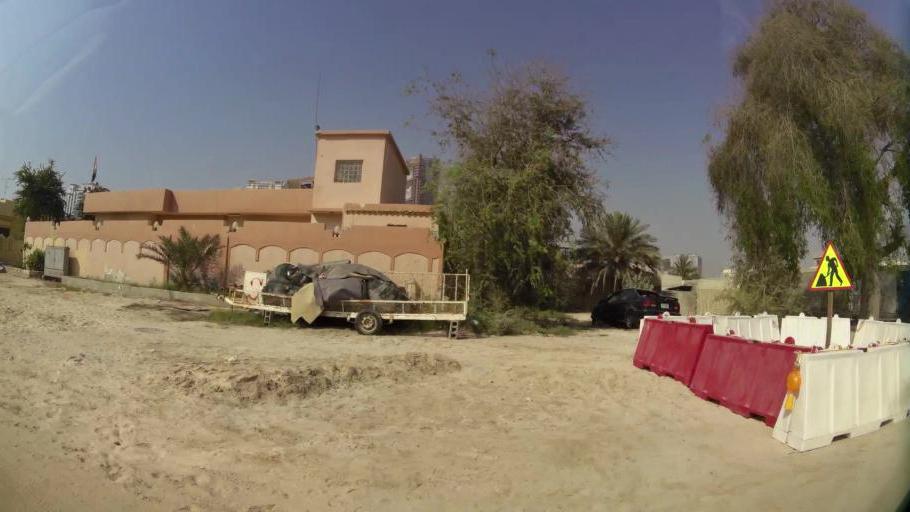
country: AE
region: Ajman
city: Ajman
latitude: 25.3898
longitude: 55.4272
